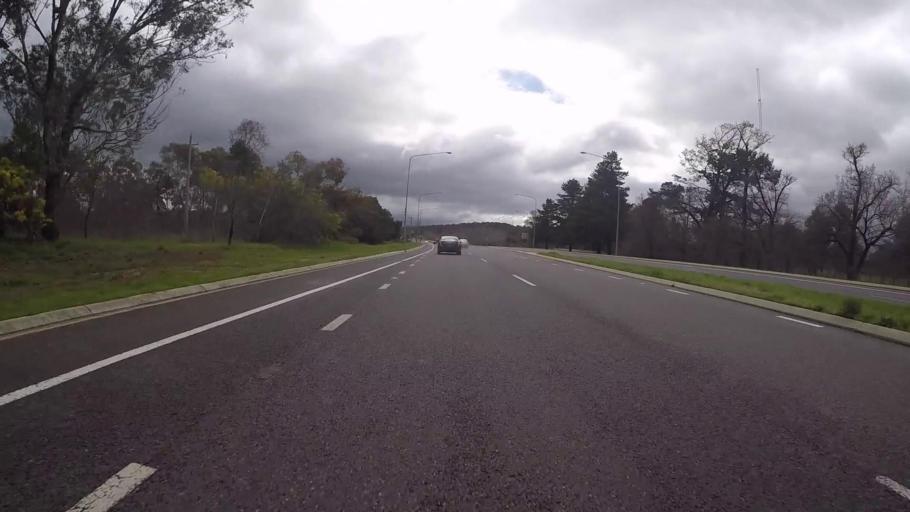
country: AU
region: Australian Capital Territory
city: Kaleen
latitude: -35.2207
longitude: 149.1198
